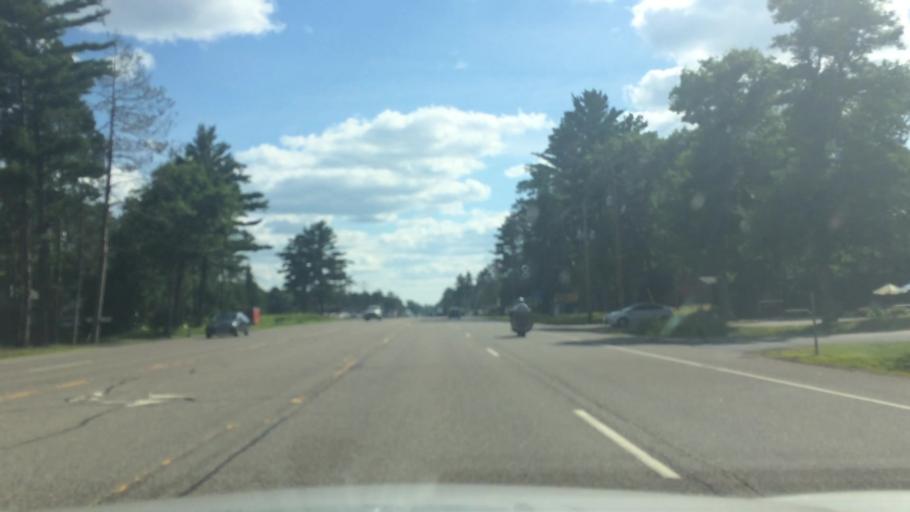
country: US
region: Wisconsin
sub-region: Vilas County
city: Lac du Flambeau
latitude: 45.8337
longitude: -89.7134
